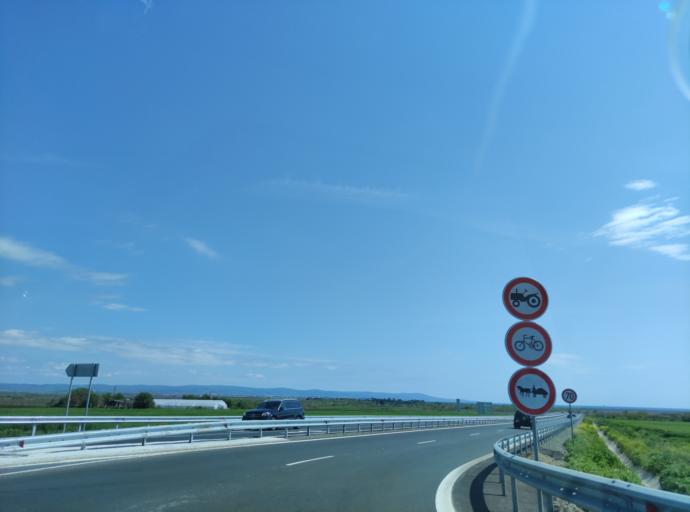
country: BG
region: Burgas
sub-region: Obshtina Pomorie
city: Pomorie
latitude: 42.5885
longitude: 27.5984
